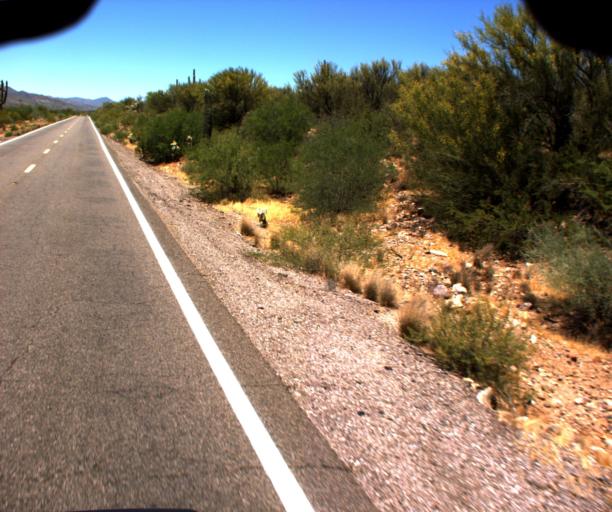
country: US
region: Arizona
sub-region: Pinal County
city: Kearny
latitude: 33.1066
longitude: -110.7559
